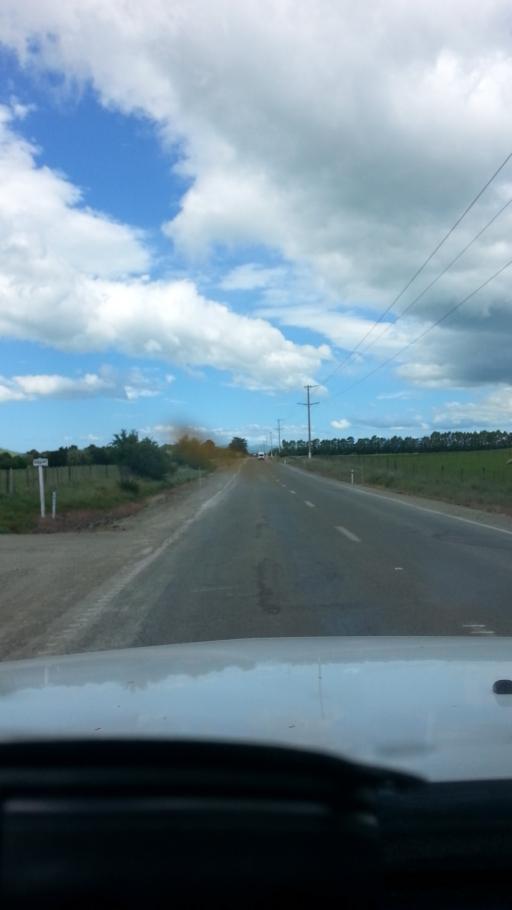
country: NZ
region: Wellington
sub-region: Masterton District
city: Masterton
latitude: -40.8289
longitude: 175.6265
